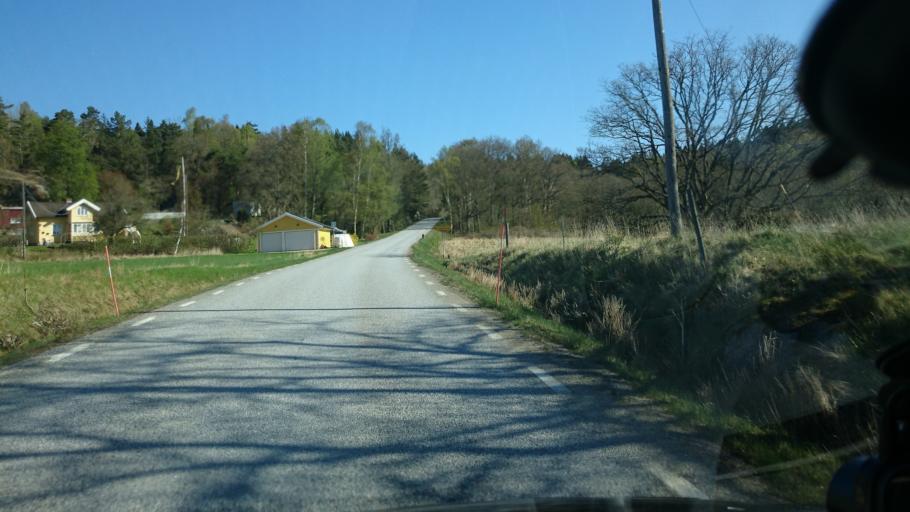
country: SE
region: Vaestra Goetaland
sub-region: Munkedals Kommun
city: Munkedal
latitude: 58.3978
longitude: 11.6532
